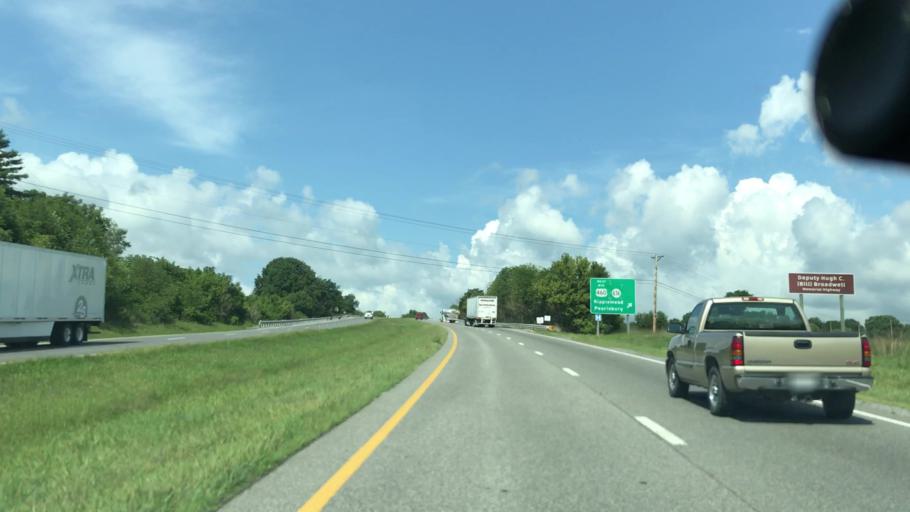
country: US
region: Virginia
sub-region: Giles County
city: Pembroke
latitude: 37.3321
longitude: -80.6854
